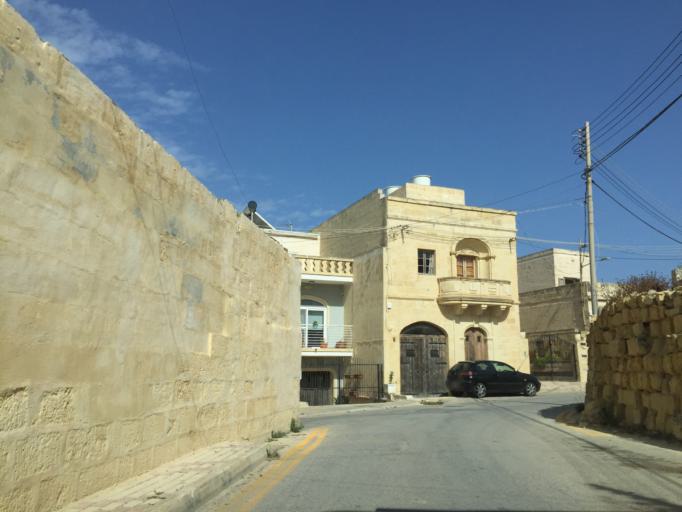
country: MT
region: L-Gharb
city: Gharb
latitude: 36.0633
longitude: 14.2088
